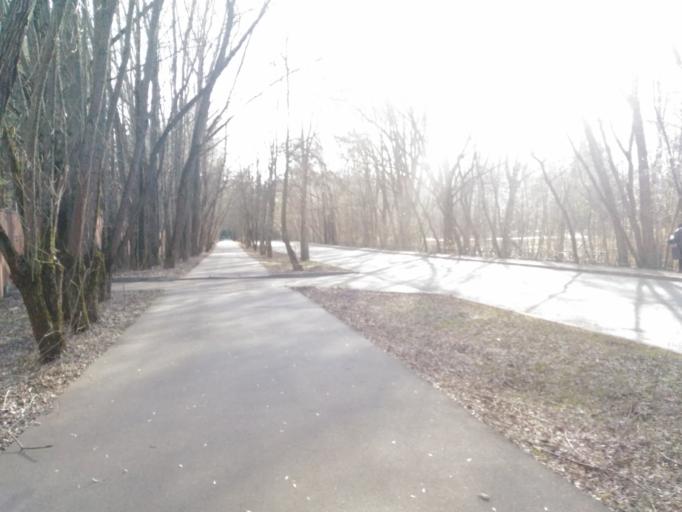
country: RU
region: Moscow
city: Strogino
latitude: 55.7883
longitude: 37.4139
